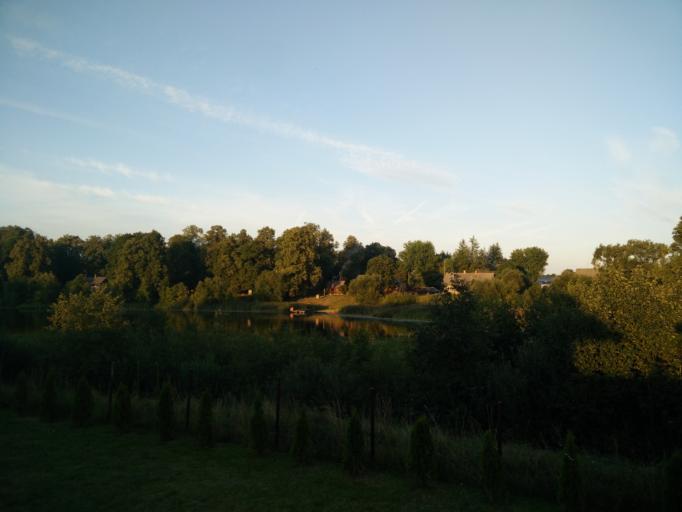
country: LT
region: Vilnius County
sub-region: Vilnius
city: Fabijoniskes
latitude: 54.8265
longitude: 25.2775
